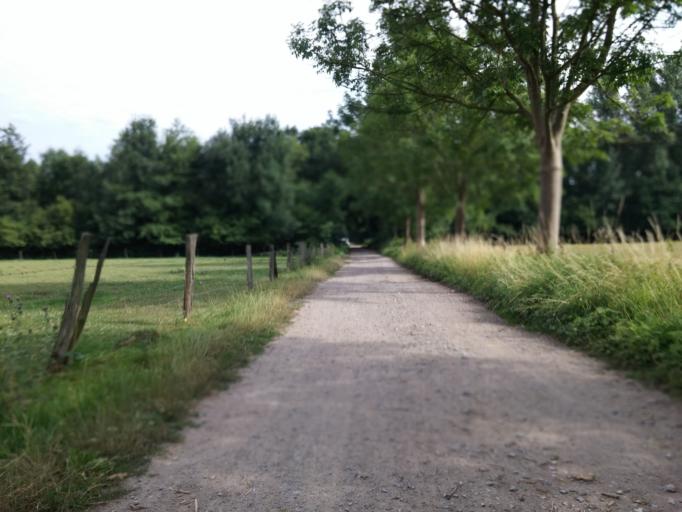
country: DE
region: North Rhine-Westphalia
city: Tonisvorst
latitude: 51.3827
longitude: 6.5283
